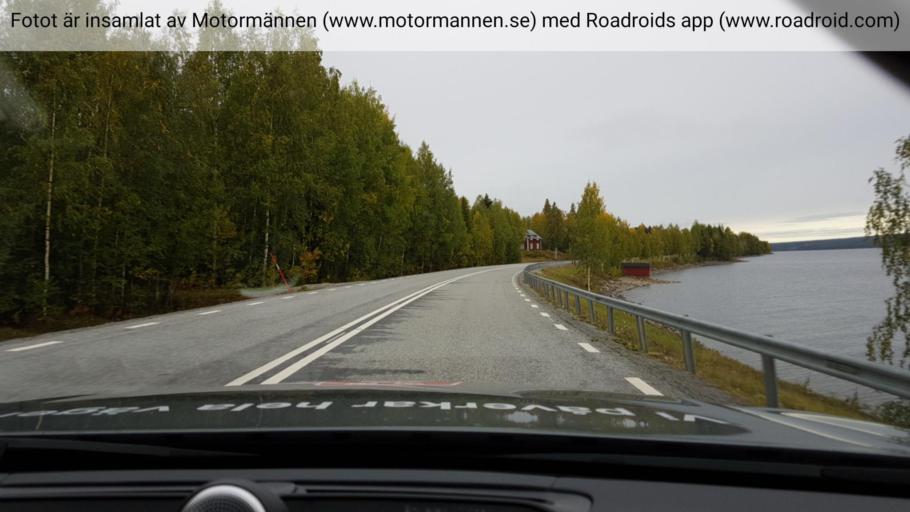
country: SE
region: Jaemtland
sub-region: Stroemsunds Kommun
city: Stroemsund
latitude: 64.1724
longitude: 15.6646
